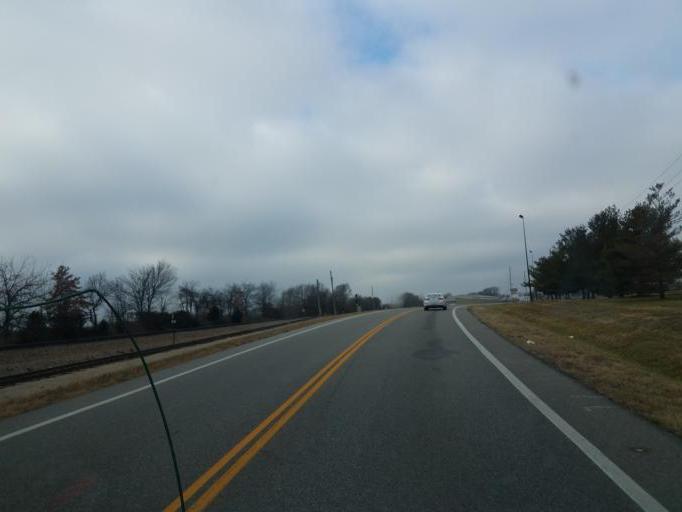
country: US
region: Missouri
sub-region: Greene County
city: Strafford
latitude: 37.2385
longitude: -93.2020
